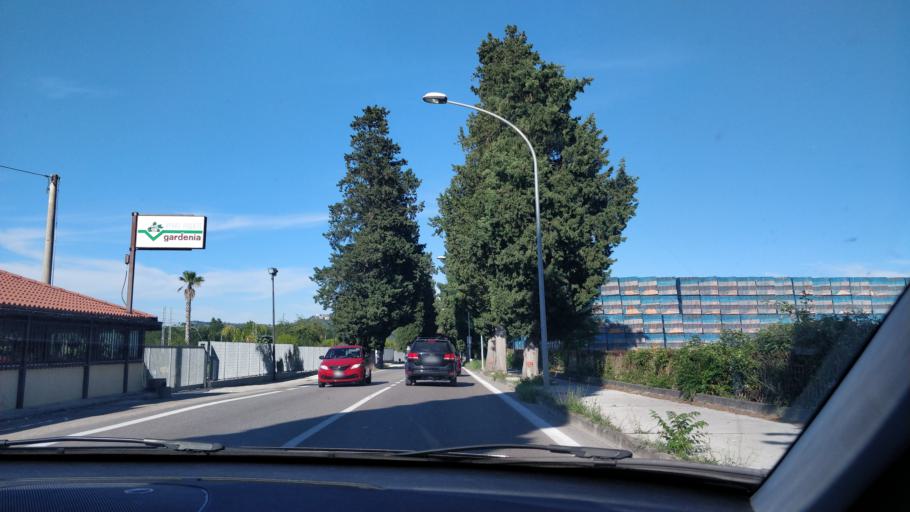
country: IT
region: Abruzzo
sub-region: Provincia di Chieti
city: Casalincontrada
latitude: 42.3288
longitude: 14.1079
